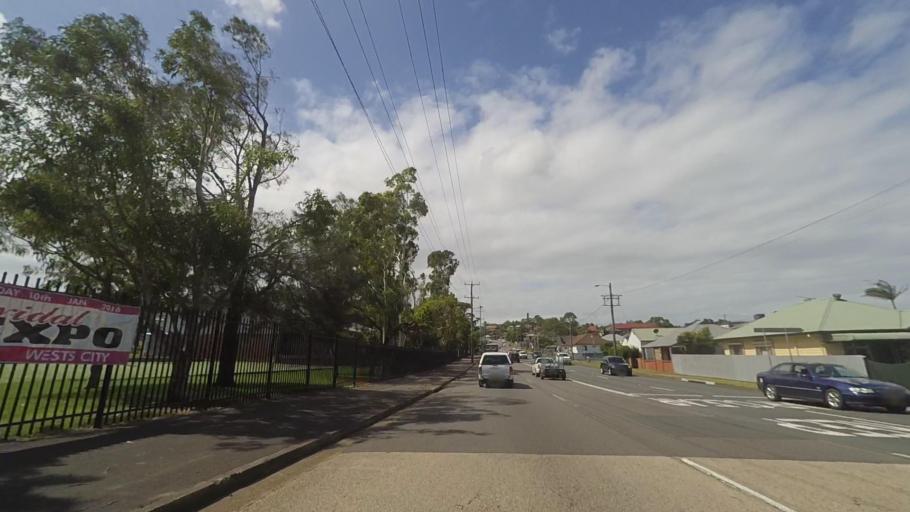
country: AU
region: New South Wales
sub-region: Newcastle
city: Lambton
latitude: -32.9125
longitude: 151.7047
